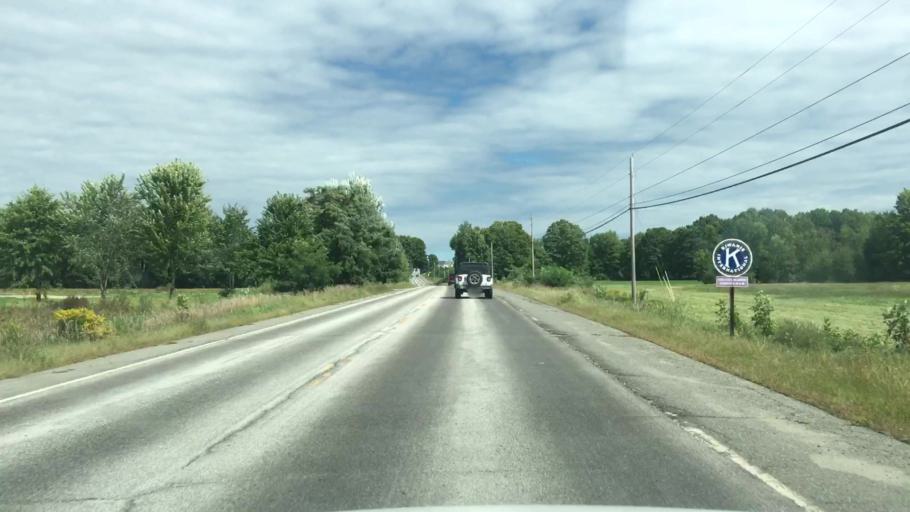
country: US
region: Maine
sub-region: Piscataquis County
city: Dover-Foxcroft
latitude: 45.1571
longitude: -69.2340
